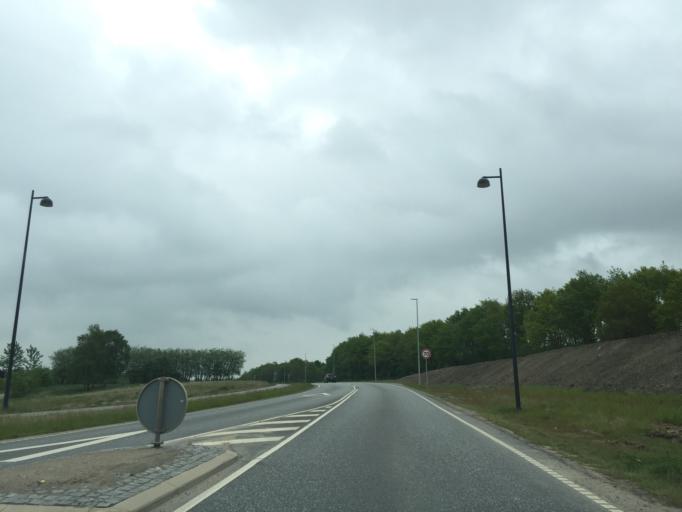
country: DK
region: Central Jutland
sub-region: Silkeborg Kommune
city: Silkeborg
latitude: 56.1973
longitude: 9.5468
